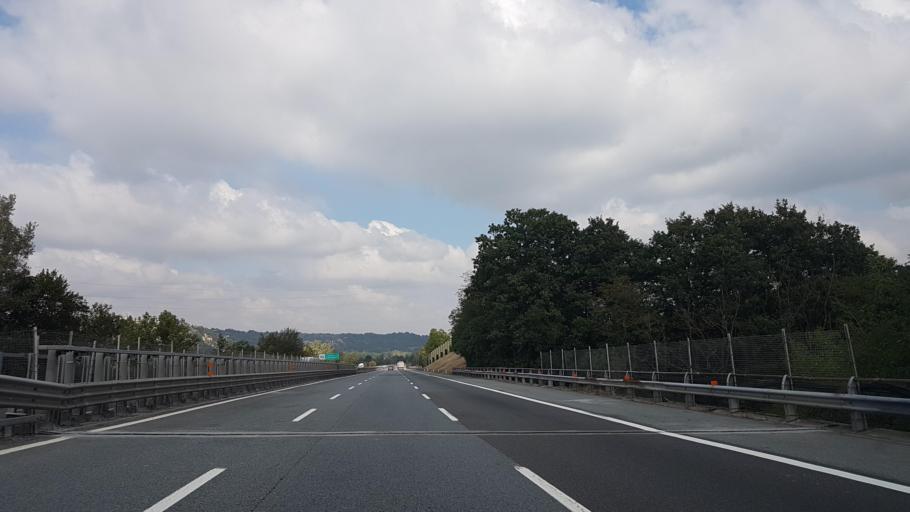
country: IT
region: Piedmont
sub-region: Provincia di Alessandria
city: Tagliolo Monferrato
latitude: 44.6550
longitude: 8.6597
